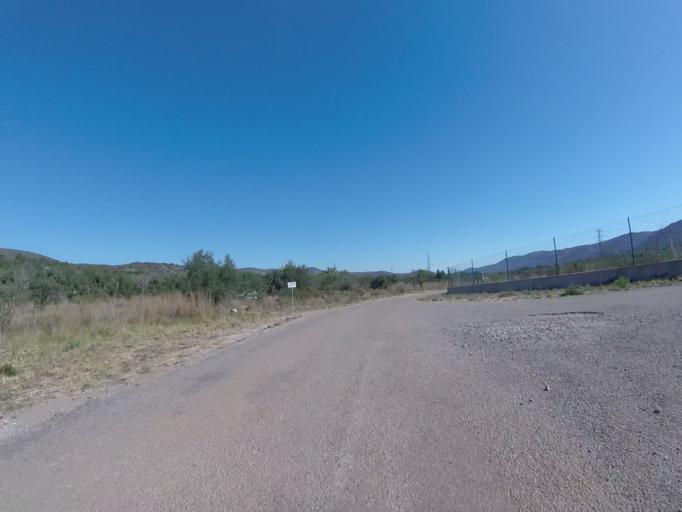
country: ES
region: Valencia
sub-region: Provincia de Castello
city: Santa Magdalena de Pulpis
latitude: 40.3476
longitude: 0.2737
